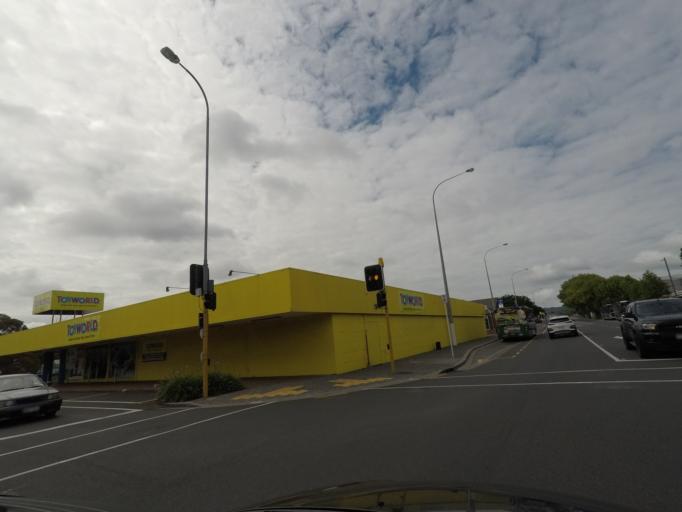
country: NZ
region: Auckland
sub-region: Auckland
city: Rosebank
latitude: -36.8818
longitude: 174.6313
